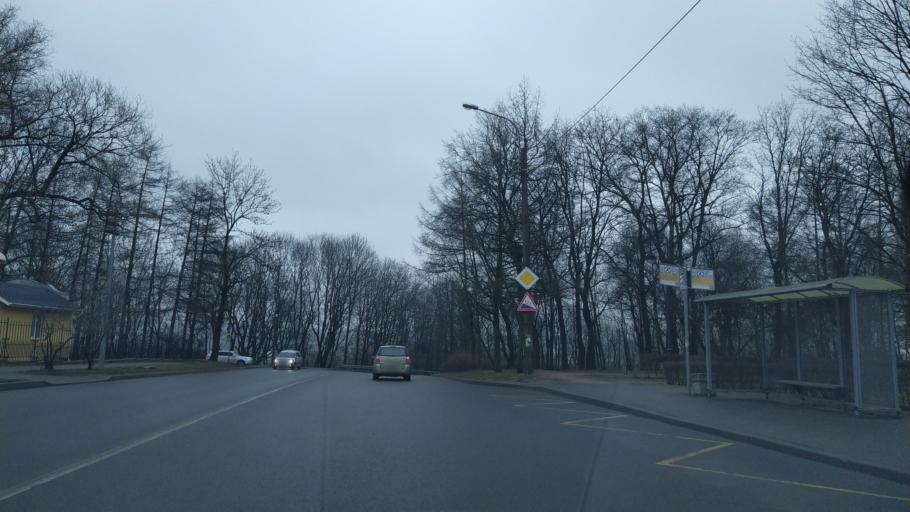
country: RU
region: St.-Petersburg
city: Krasnoye Selo
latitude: 59.7329
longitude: 30.0884
